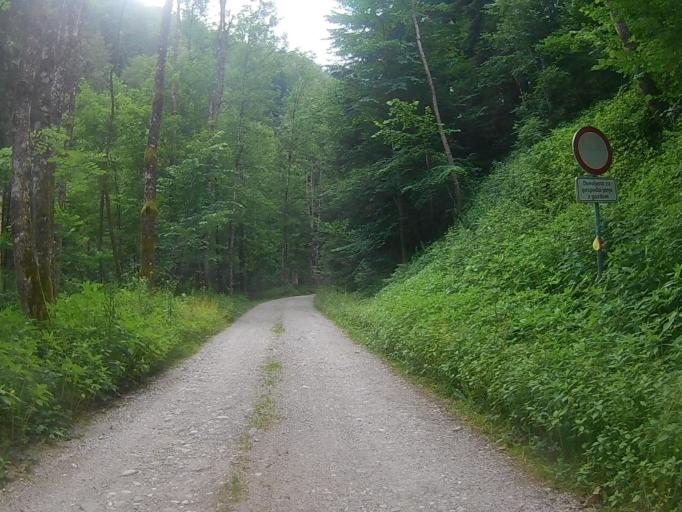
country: SI
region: Selnica ob Dravi
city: Selnica ob Dravi
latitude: 46.5230
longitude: 15.4599
